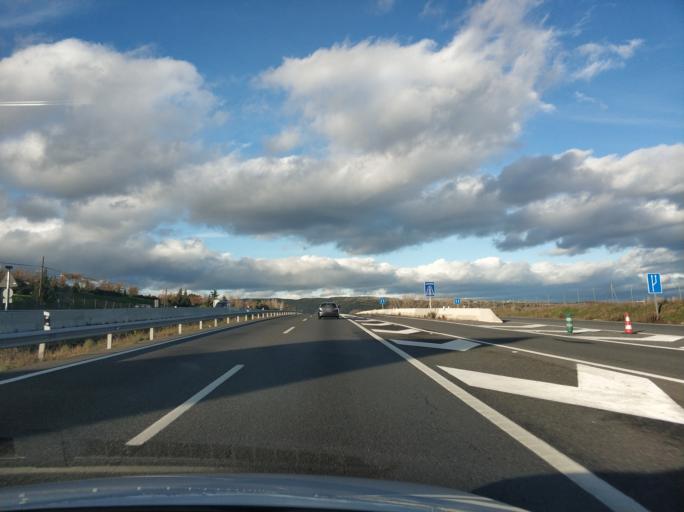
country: ES
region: Madrid
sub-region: Provincia de Madrid
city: San Agustin de Guadalix
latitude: 40.6763
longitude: -3.6113
